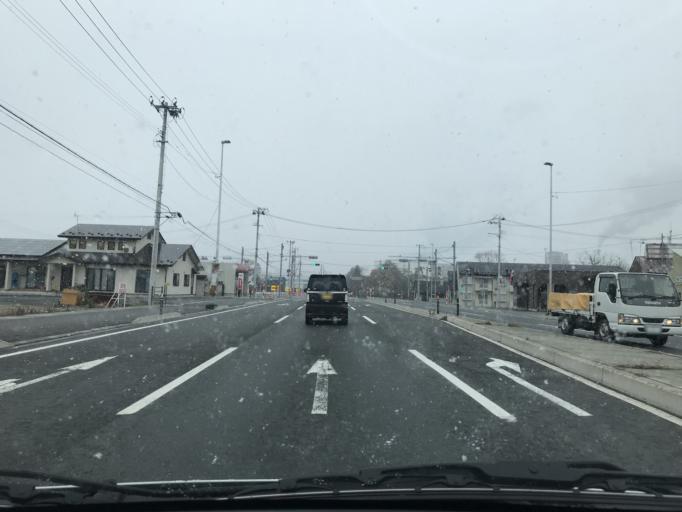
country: JP
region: Iwate
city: Kitakami
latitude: 39.2265
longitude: 141.0946
